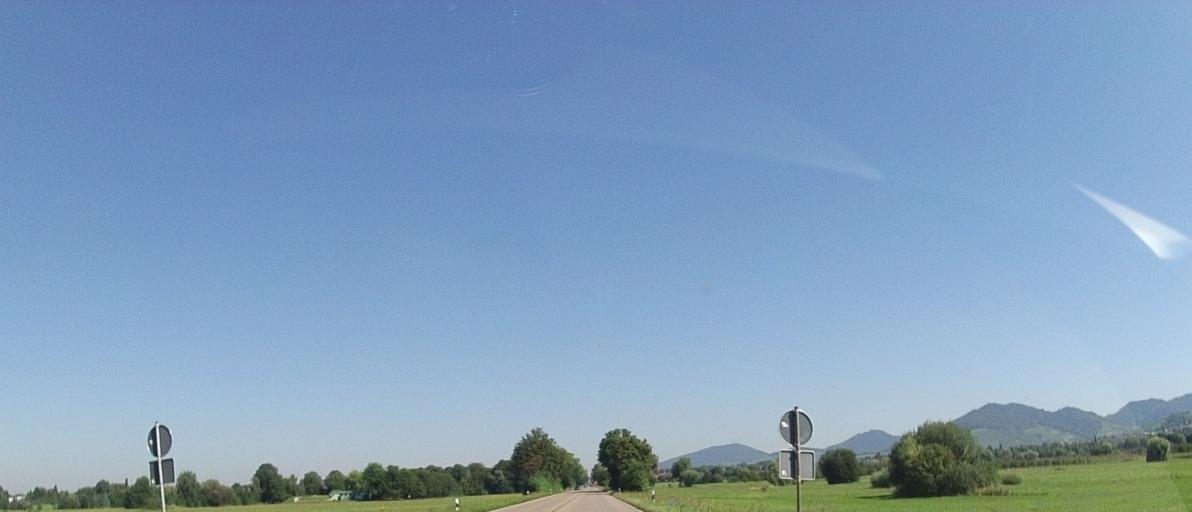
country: DE
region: Baden-Wuerttemberg
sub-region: Karlsruhe Region
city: Buhl
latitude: 48.6818
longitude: 8.1264
